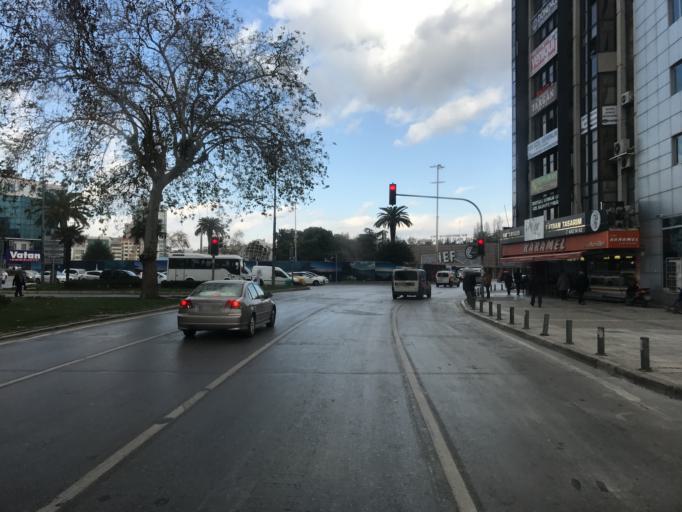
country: TR
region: Izmir
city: Izmir
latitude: 38.4229
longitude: 27.1434
